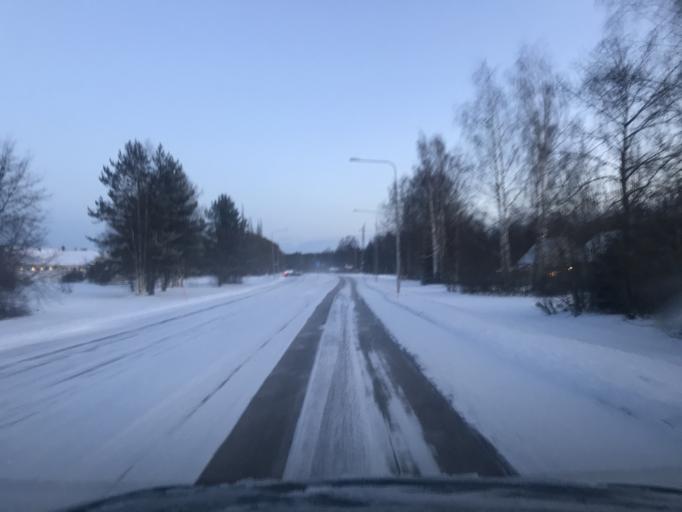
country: SE
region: Norrbotten
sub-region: Lulea Kommun
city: Sodra Sunderbyn
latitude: 65.6523
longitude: 21.9636
